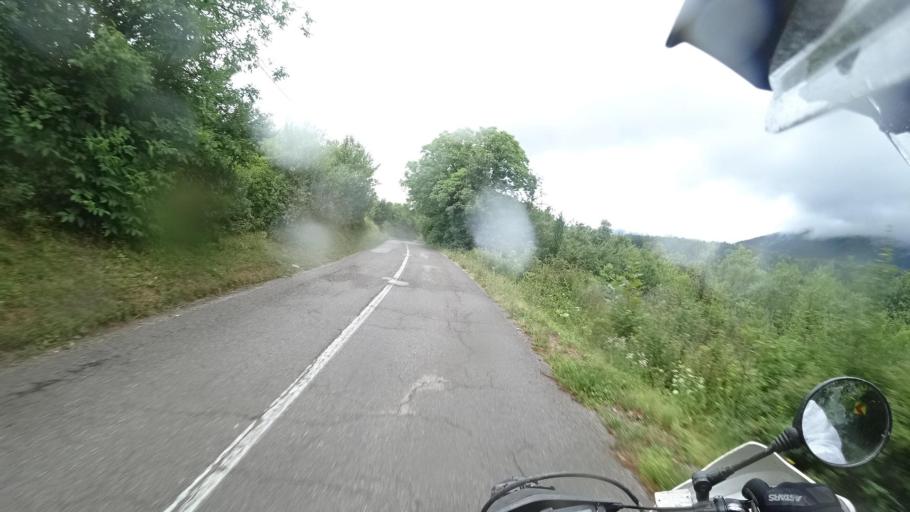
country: HR
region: Karlovacka
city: Plaski
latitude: 45.0148
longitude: 15.4171
